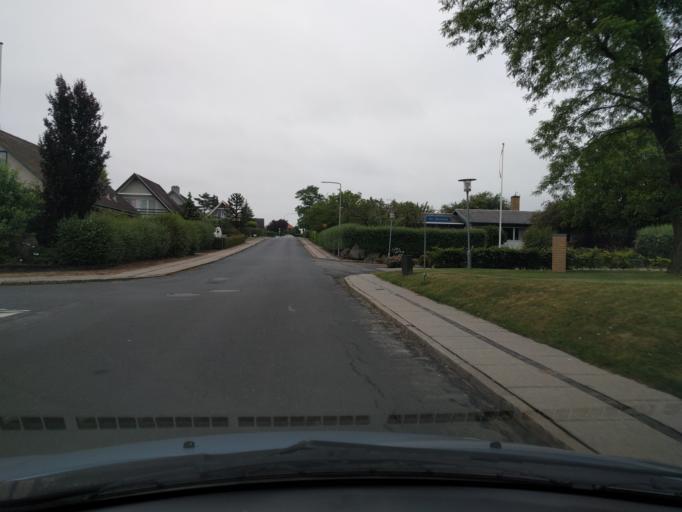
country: DK
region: South Denmark
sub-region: Kerteminde Kommune
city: Kerteminde
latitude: 55.4520
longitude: 10.6471
